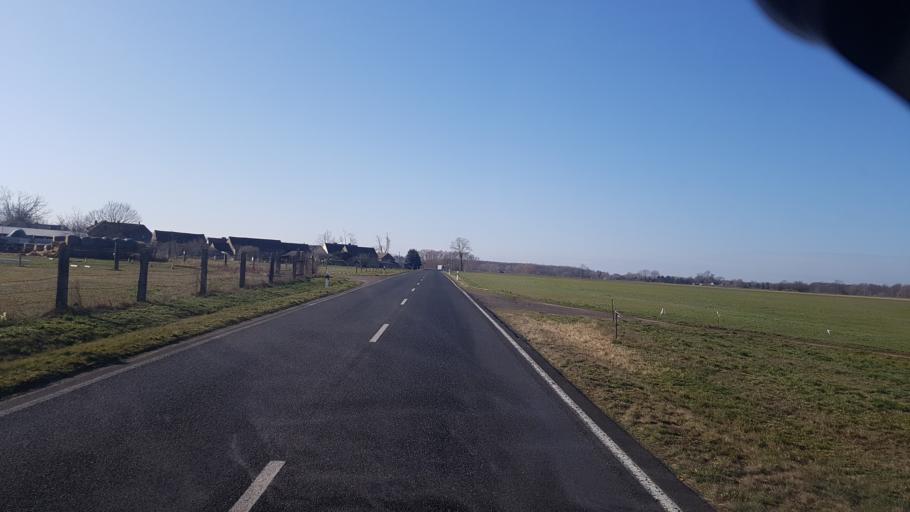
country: DE
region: Brandenburg
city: Luebben
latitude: 51.8553
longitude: 13.8450
